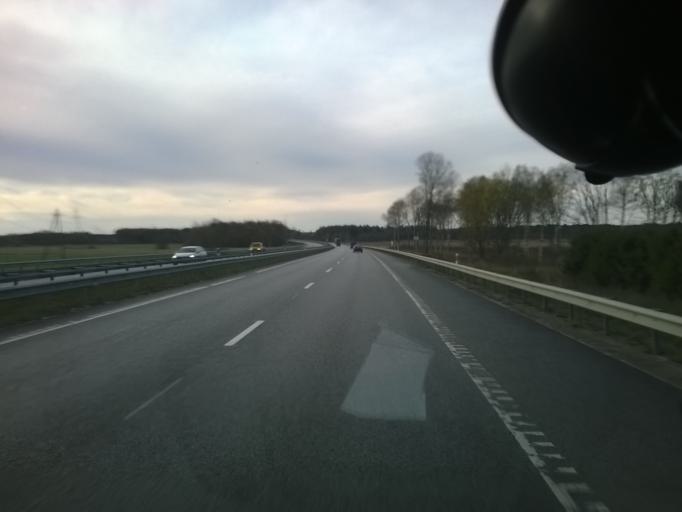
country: EE
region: Harju
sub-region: Kiili vald
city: Kiili
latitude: 59.3345
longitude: 24.8078
